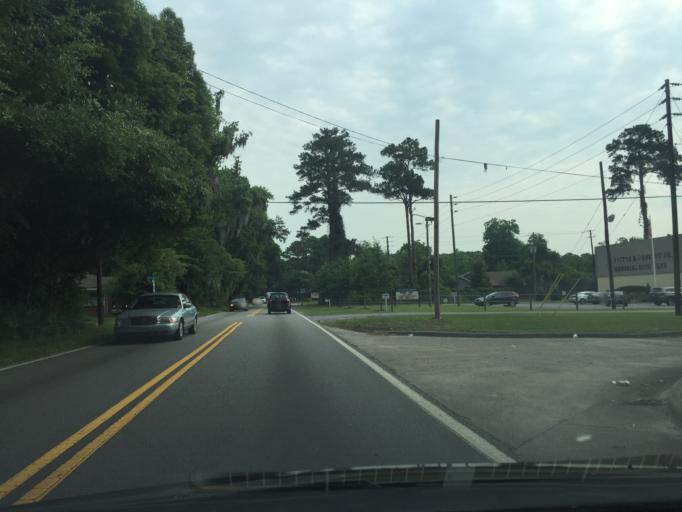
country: US
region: Georgia
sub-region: Chatham County
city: Isle of Hope
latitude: 32.0121
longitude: -81.0991
